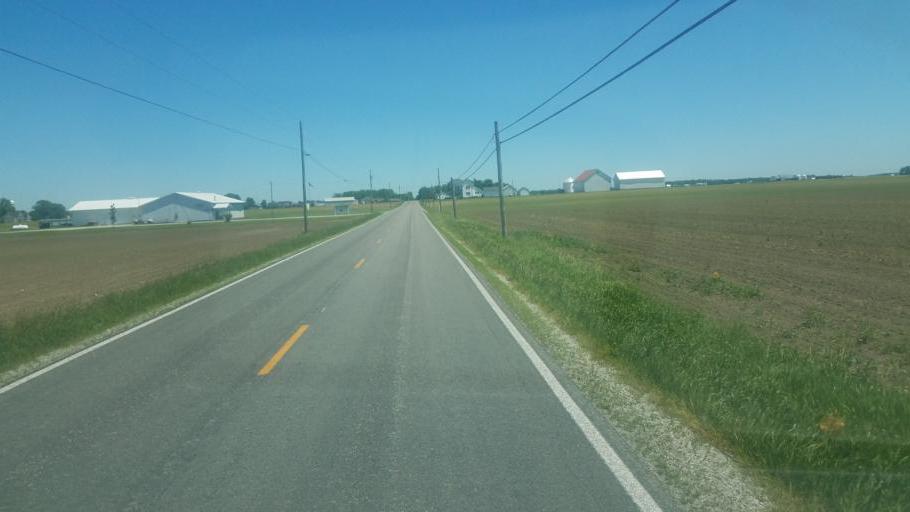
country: US
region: Ohio
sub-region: Darke County
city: Versailles
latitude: 40.2264
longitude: -84.4252
